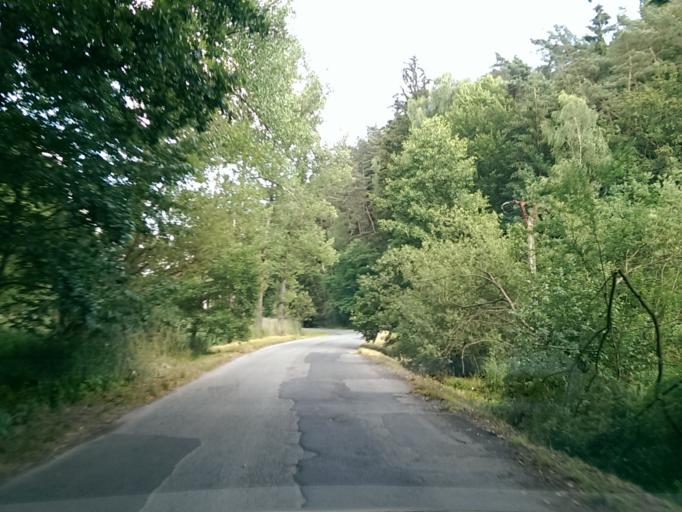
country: CZ
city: Duba
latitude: 50.5306
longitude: 14.5639
